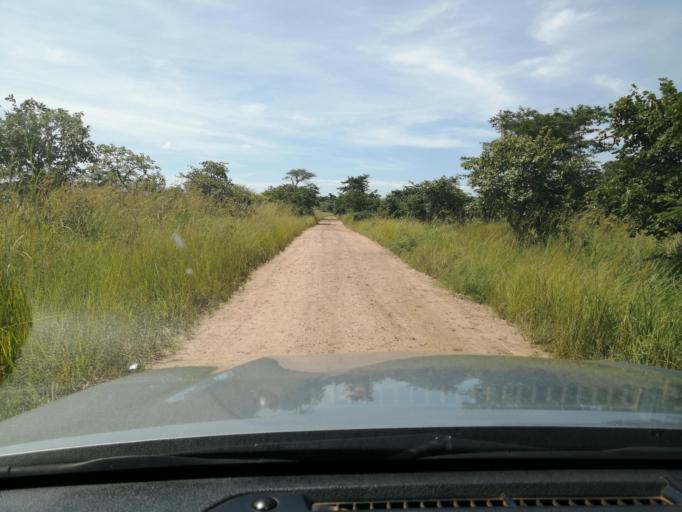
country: ZM
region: Central
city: Chibombo
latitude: -15.0029
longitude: 27.8234
